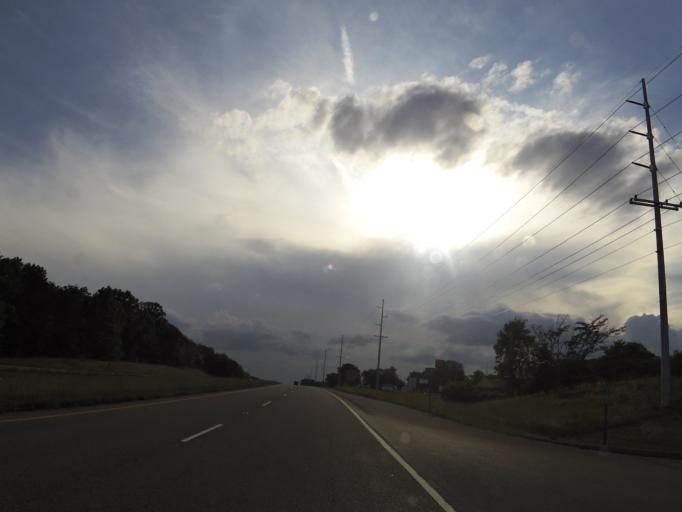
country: US
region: Tennessee
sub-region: Blount County
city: Wildwood
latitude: 35.7595
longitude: -83.8656
